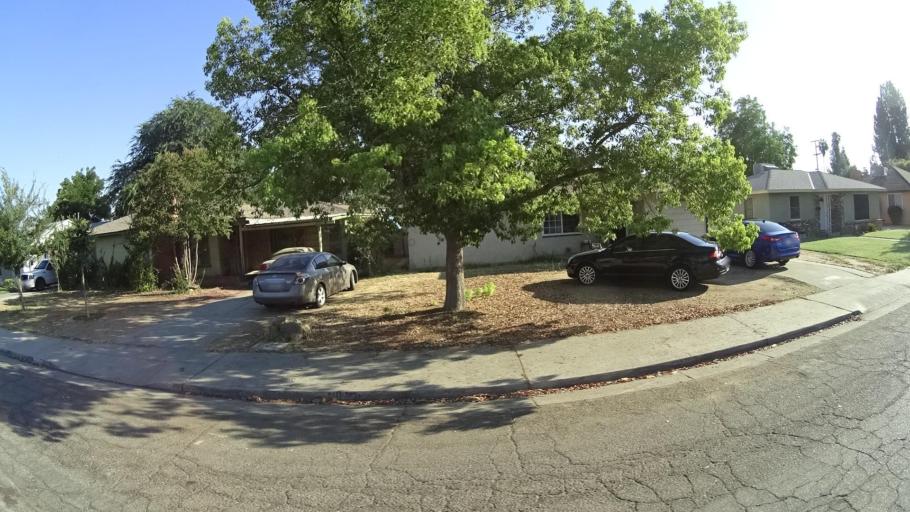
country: US
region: California
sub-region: Fresno County
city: Fresno
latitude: 36.7732
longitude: -119.7623
